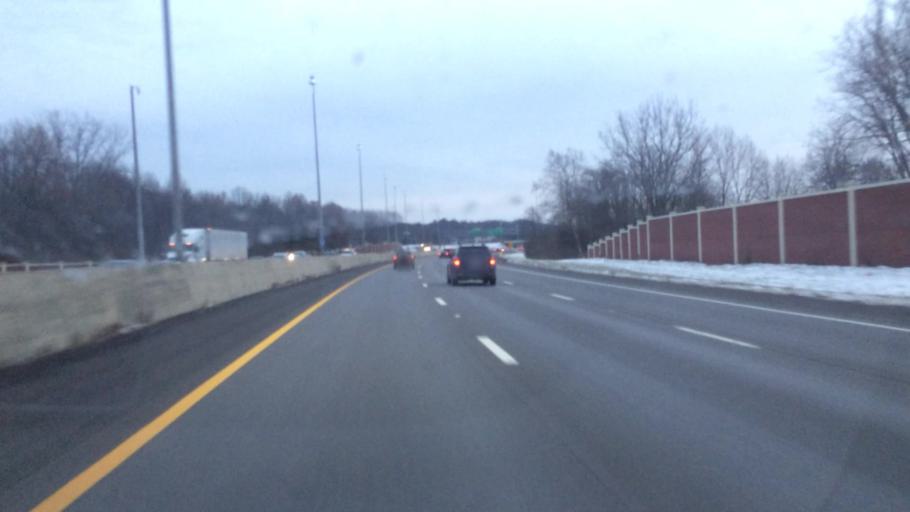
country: US
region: Ohio
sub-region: Summit County
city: Fairlawn
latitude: 41.1174
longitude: -81.6173
